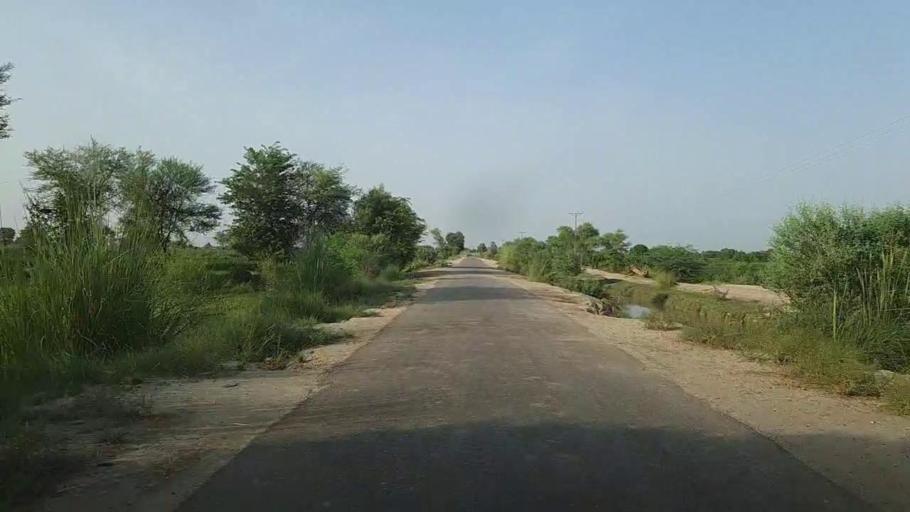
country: PK
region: Sindh
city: Khairpur
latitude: 28.0863
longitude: 69.8171
